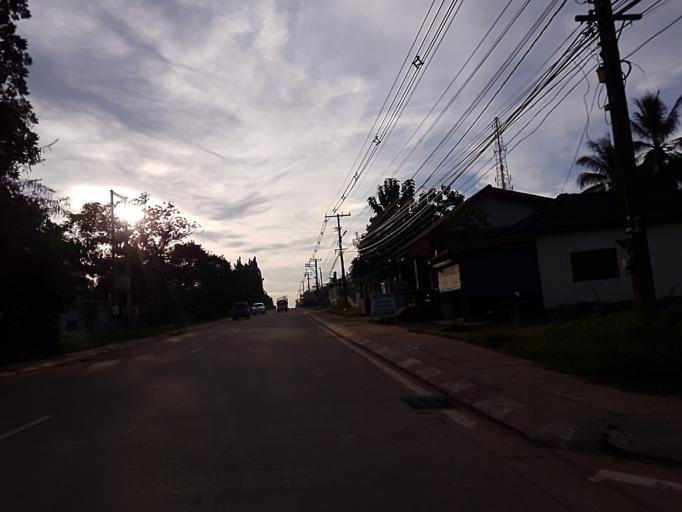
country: TH
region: Nong Khai
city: Si Chiang Mai
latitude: 18.0199
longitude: 102.5194
